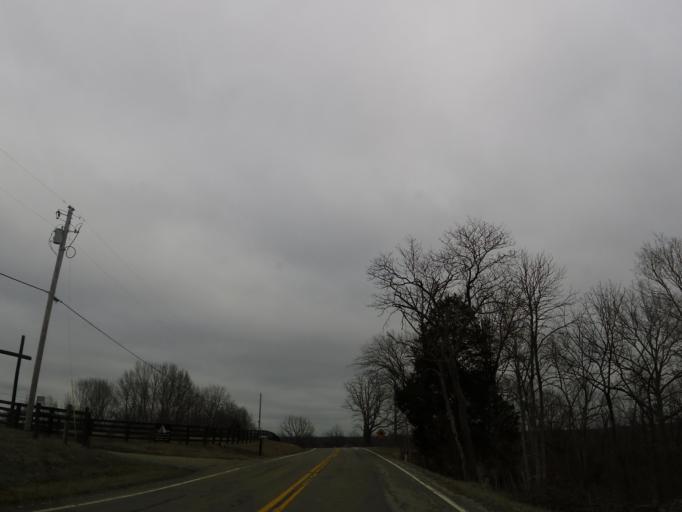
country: US
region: Kentucky
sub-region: Henry County
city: Eminence
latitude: 38.3463
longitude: -85.0107
